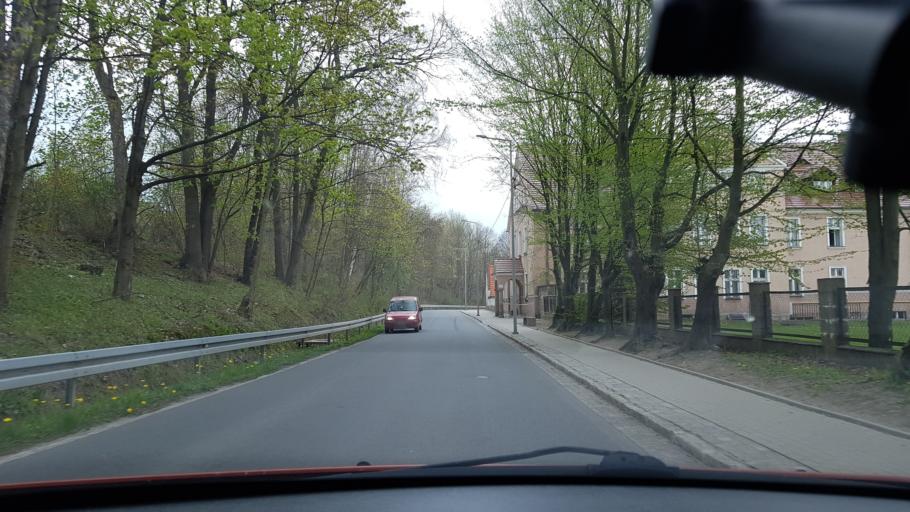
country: PL
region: Lower Silesian Voivodeship
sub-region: Powiat klodzki
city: Klodzko
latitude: 50.4273
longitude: 16.6446
